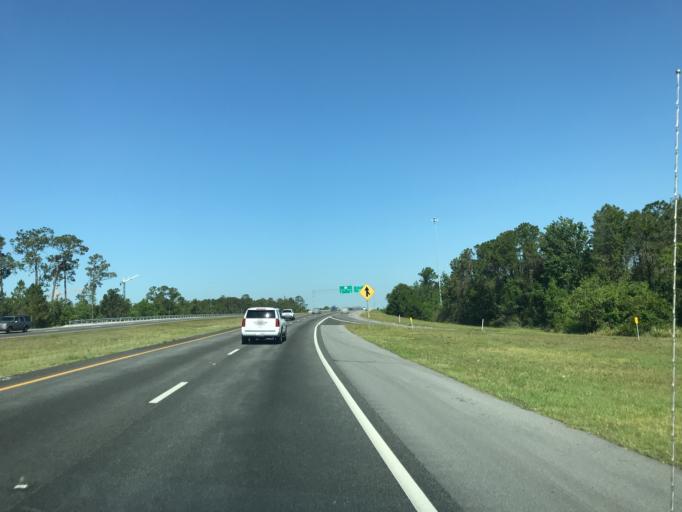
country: US
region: Florida
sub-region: Osceola County
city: Celebration
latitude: 28.3588
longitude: -81.5171
